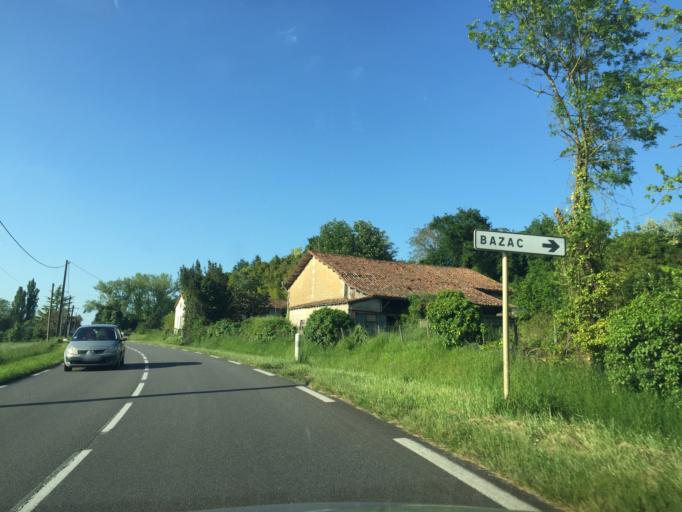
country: FR
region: Poitou-Charentes
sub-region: Departement de la Charente
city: Chalais
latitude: 45.2308
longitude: 0.0364
